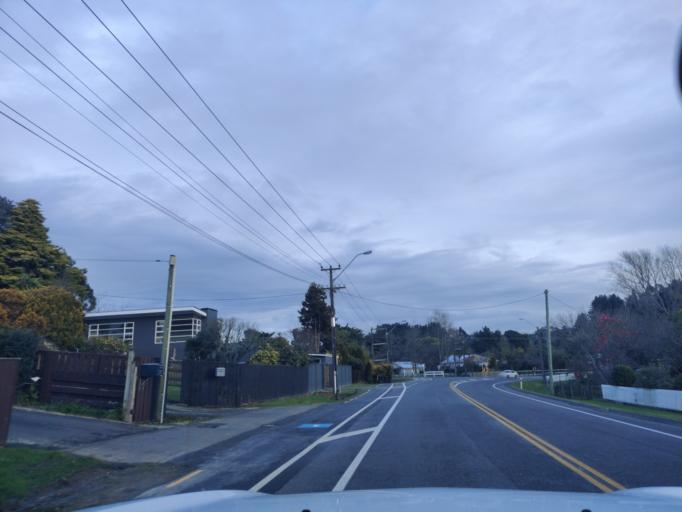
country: NZ
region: Manawatu-Wanganui
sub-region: Palmerston North City
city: Palmerston North
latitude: -40.3751
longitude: 175.6508
